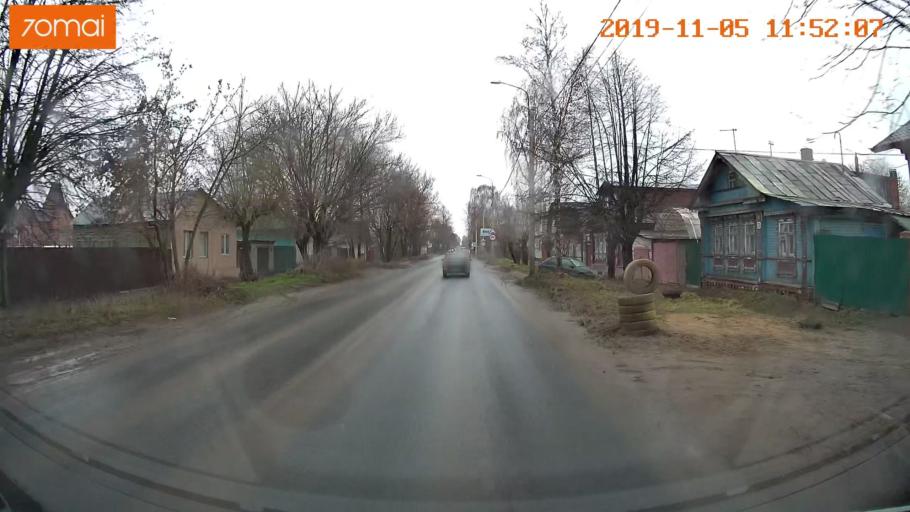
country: RU
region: Ivanovo
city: Bogorodskoye
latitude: 57.0016
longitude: 41.0291
